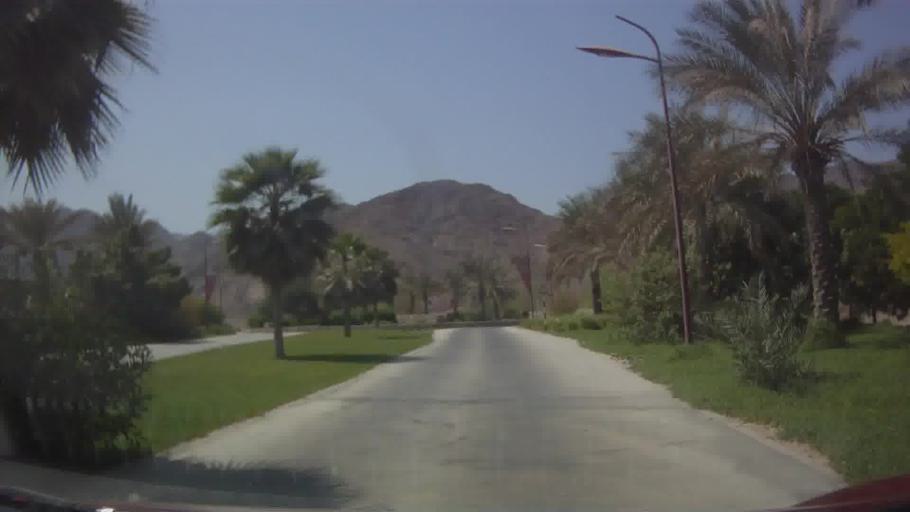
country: OM
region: Muhafazat Masqat
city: Muscat
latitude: 23.4135
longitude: 58.7859
